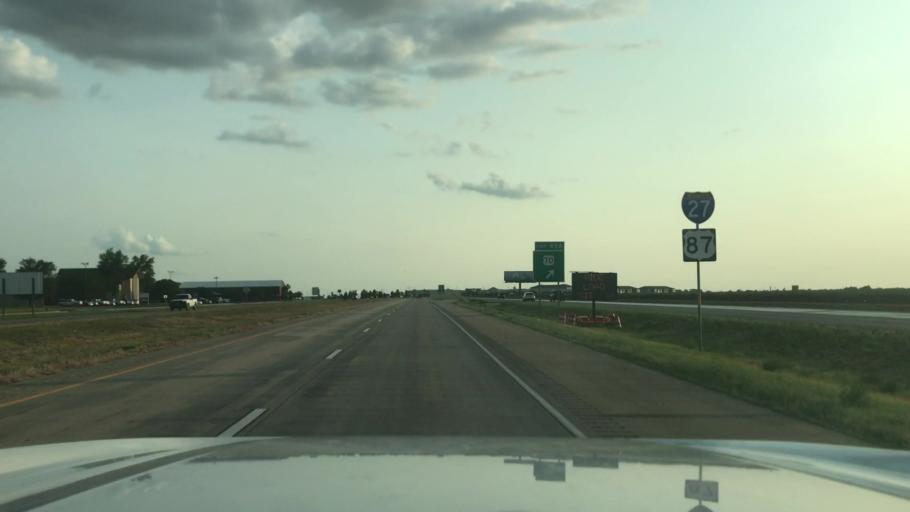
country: US
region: Texas
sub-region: Hale County
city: Plainview
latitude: 34.2029
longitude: -101.7439
